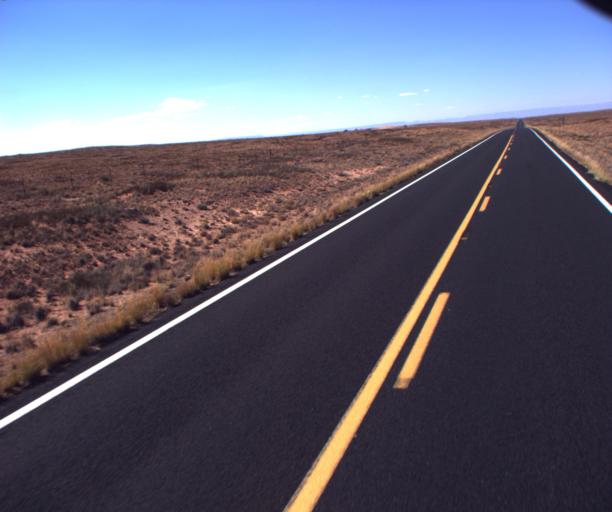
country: US
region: Arizona
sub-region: Coconino County
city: Tuba City
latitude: 36.0160
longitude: -111.0967
